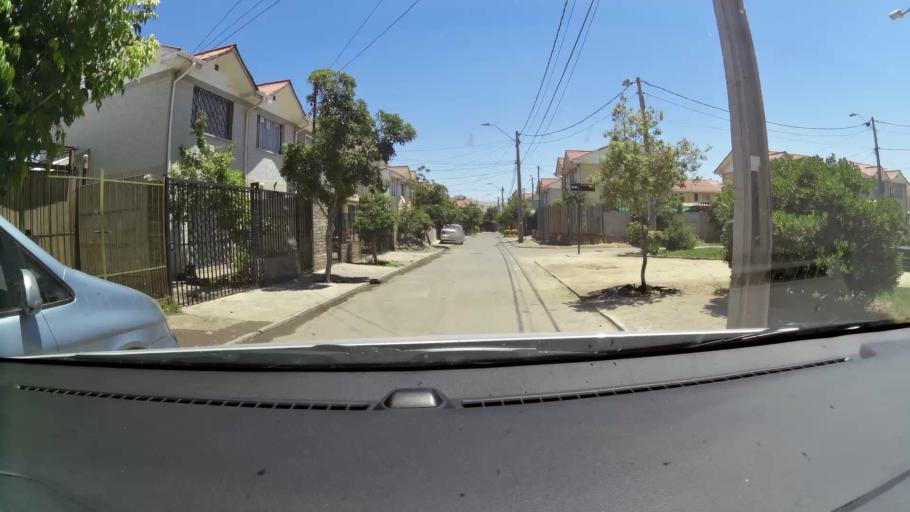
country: CL
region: Santiago Metropolitan
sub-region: Provincia de Maipo
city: San Bernardo
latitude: -33.6048
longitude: -70.6722
